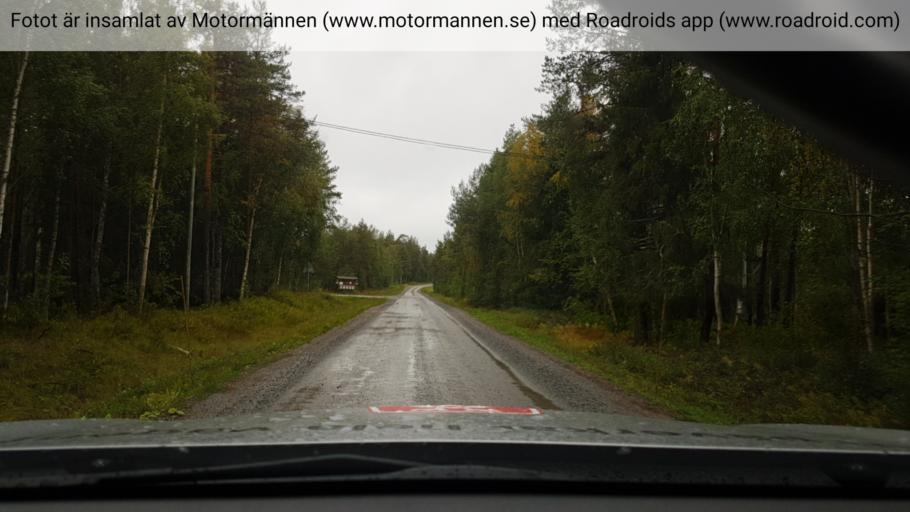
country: SE
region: Vaesterbotten
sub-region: Asele Kommun
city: Asele
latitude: 64.0201
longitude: 17.6542
